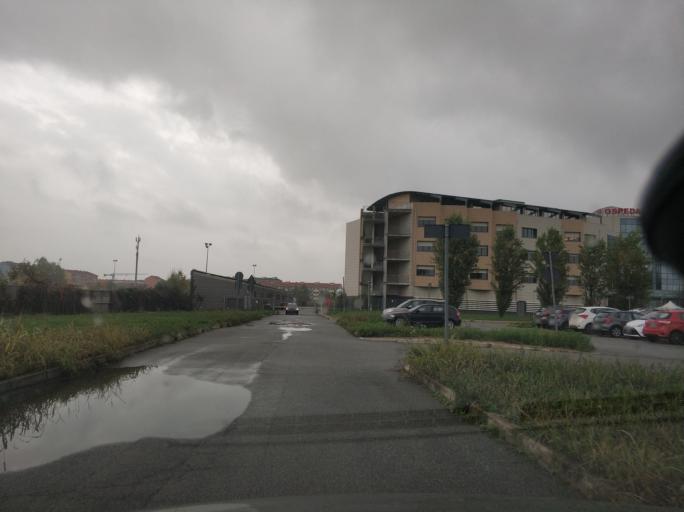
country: IT
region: Piedmont
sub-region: Provincia di Torino
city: Settimo Torinese
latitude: 45.1254
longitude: 7.7543
